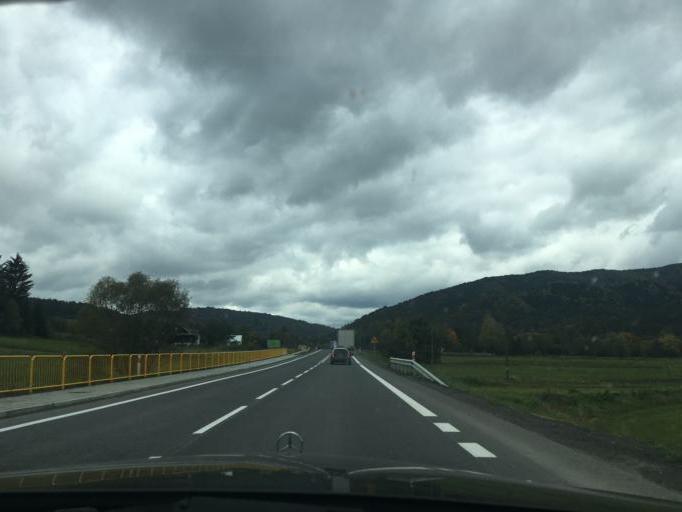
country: PL
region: Subcarpathian Voivodeship
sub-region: Powiat krosnienski
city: Dukla
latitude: 49.5060
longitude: 21.6979
